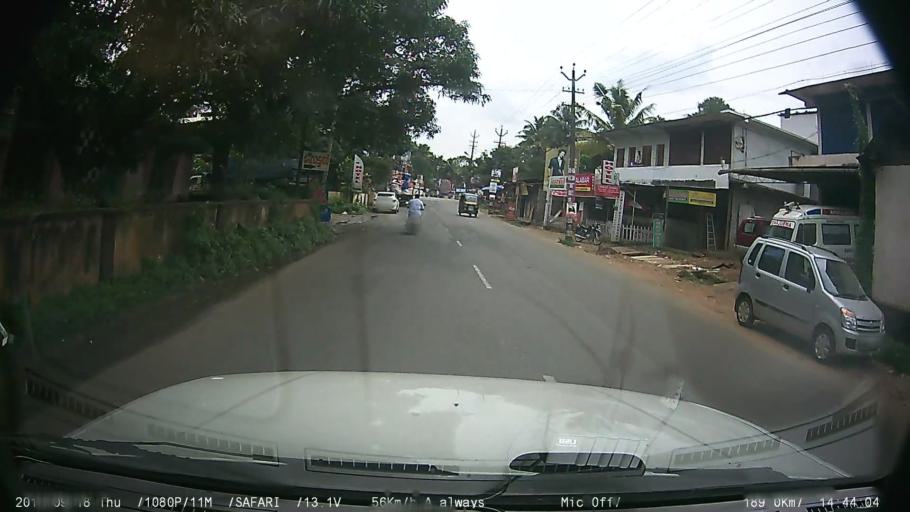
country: IN
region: Kerala
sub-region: Ernakulam
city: Muvattupula
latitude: 9.9971
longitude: 76.5975
